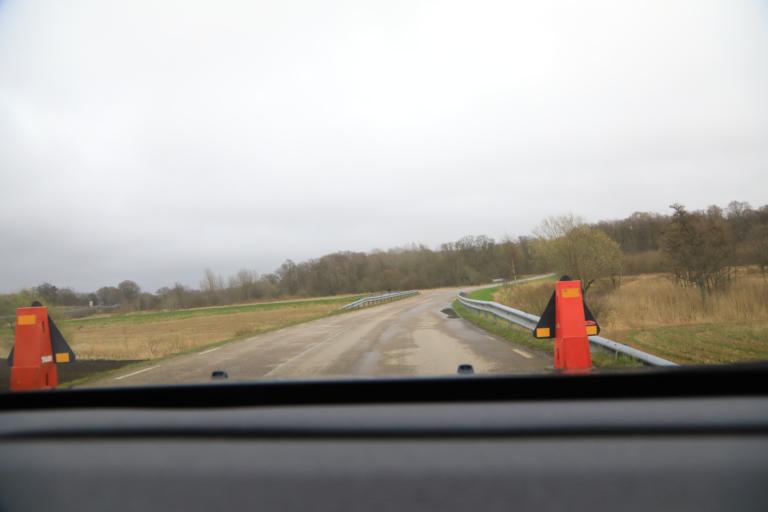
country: SE
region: Halland
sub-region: Kungsbacka Kommun
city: Frillesas
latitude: 57.2973
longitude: 12.2105
